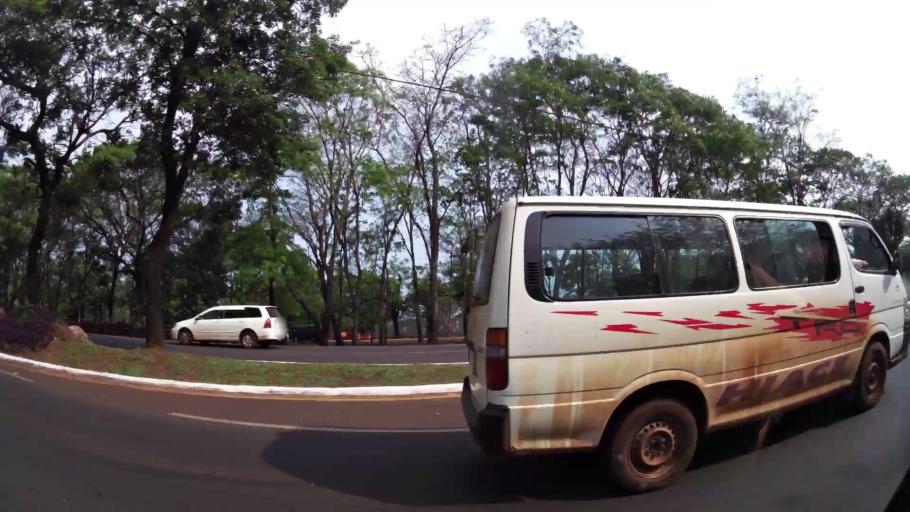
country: PY
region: Alto Parana
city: Ciudad del Este
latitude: -25.5107
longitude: -54.6230
